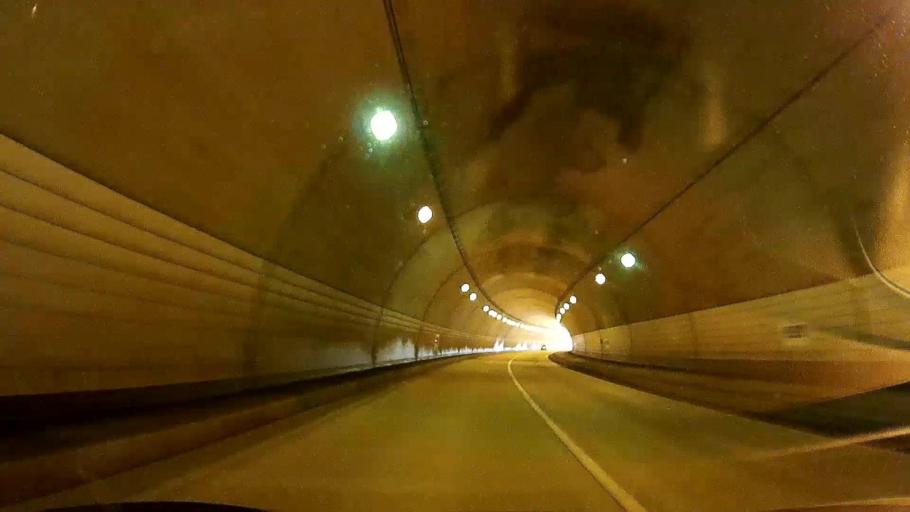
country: JP
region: Niigata
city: Tokamachi
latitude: 37.0040
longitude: 138.6389
